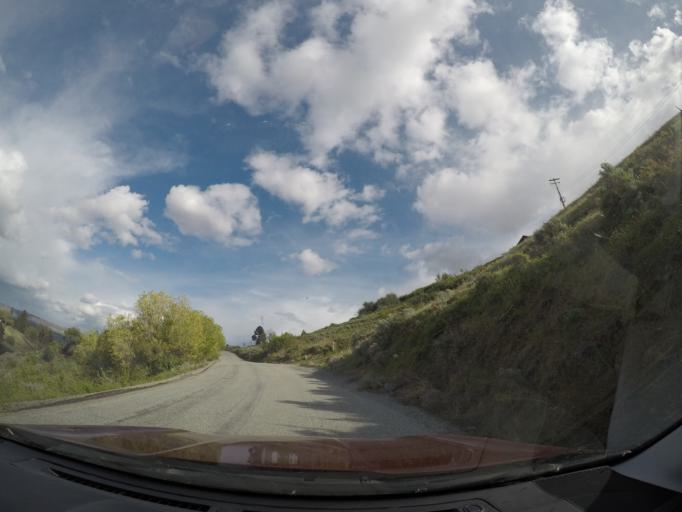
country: US
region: Washington
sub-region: Chelan County
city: Sunnyslope
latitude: 47.4605
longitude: -120.3465
